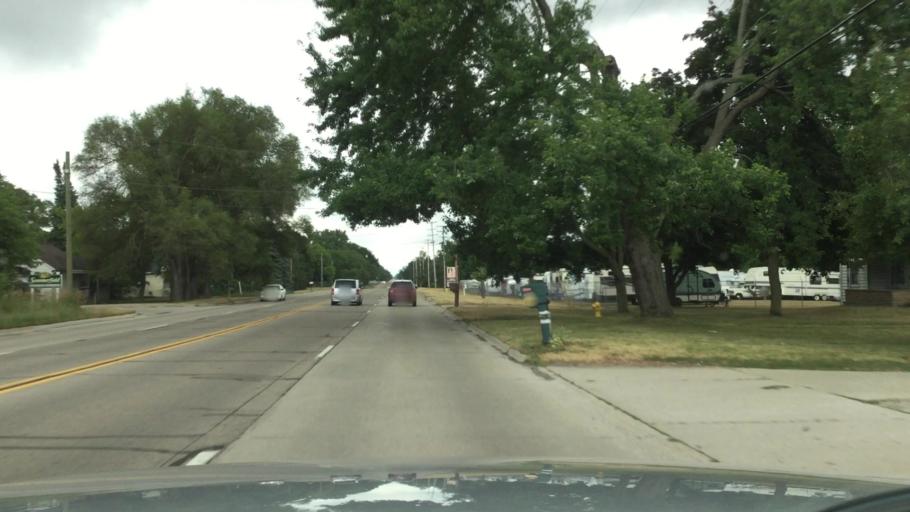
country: US
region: Michigan
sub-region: Genesee County
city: Beecher
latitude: 43.0829
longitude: -83.6170
